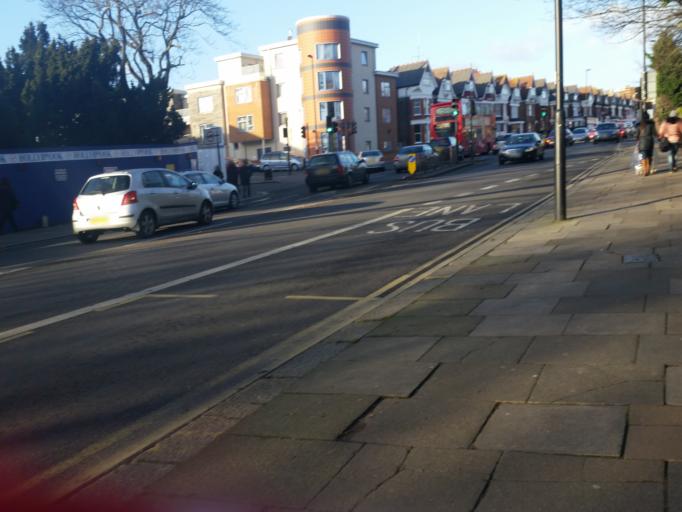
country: GB
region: England
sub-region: Greater London
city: Wood Green
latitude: 51.6152
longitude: -0.1095
